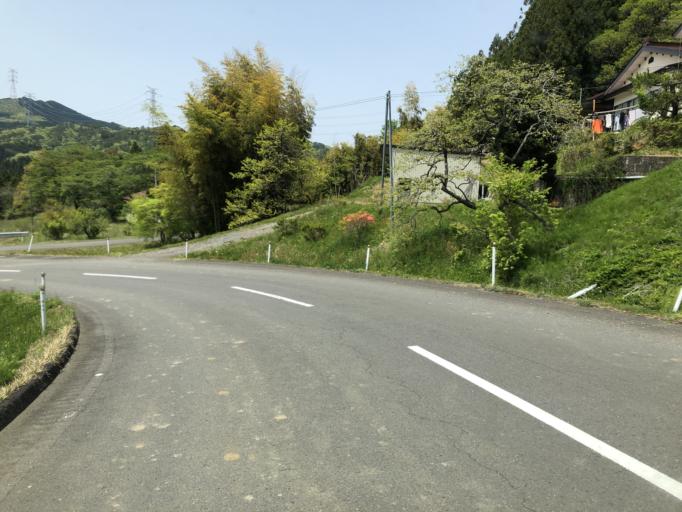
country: JP
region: Fukushima
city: Ishikawa
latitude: 37.0145
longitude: 140.3569
